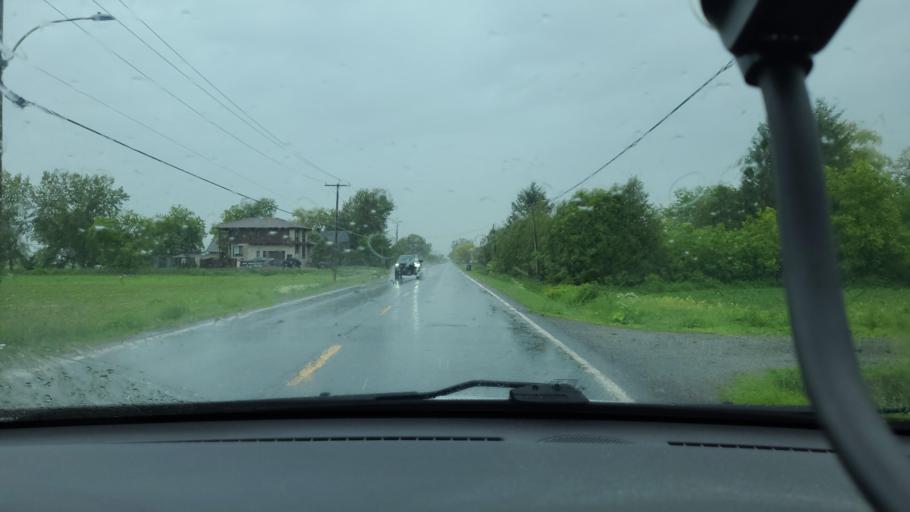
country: CA
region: Quebec
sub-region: Monteregie
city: Saint-Hyacinthe
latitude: 45.6171
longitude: -73.0093
